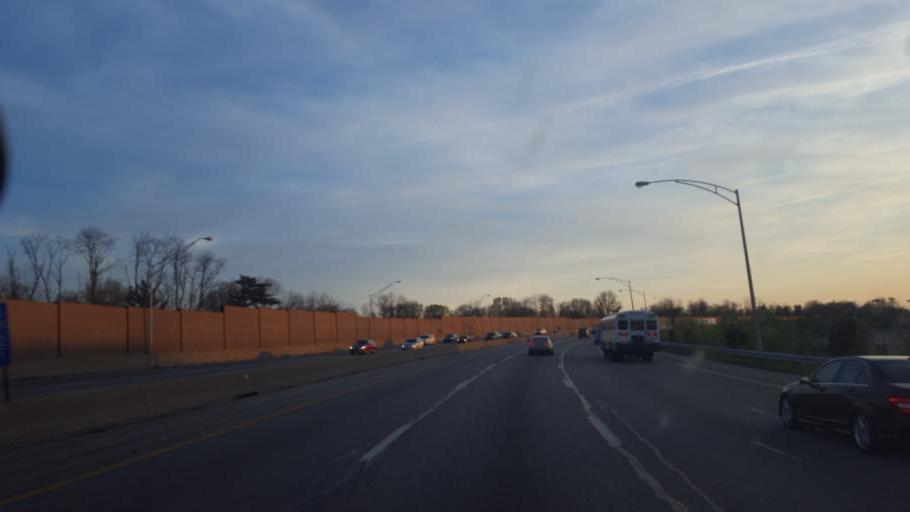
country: US
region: Ohio
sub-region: Hamilton County
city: Madeira
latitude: 39.1974
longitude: -84.3762
